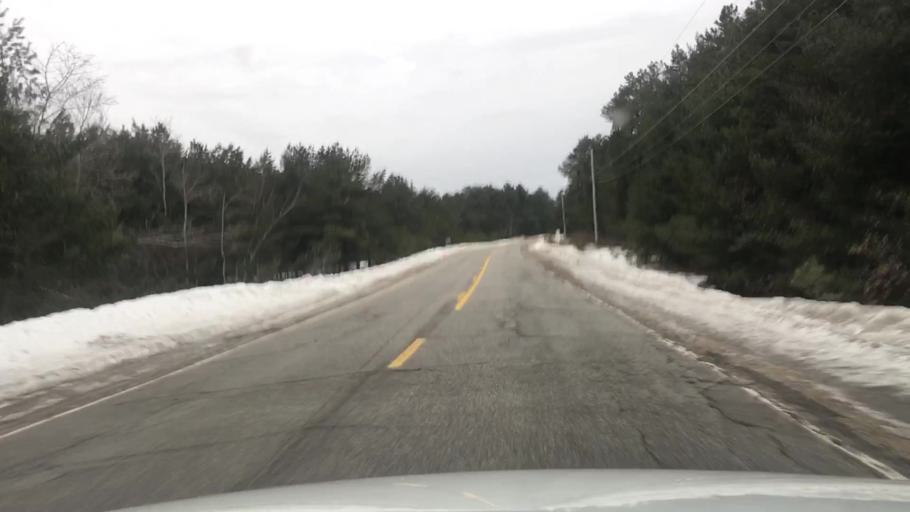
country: US
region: Maine
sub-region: York County
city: Newfield
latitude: 43.5960
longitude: -70.8810
